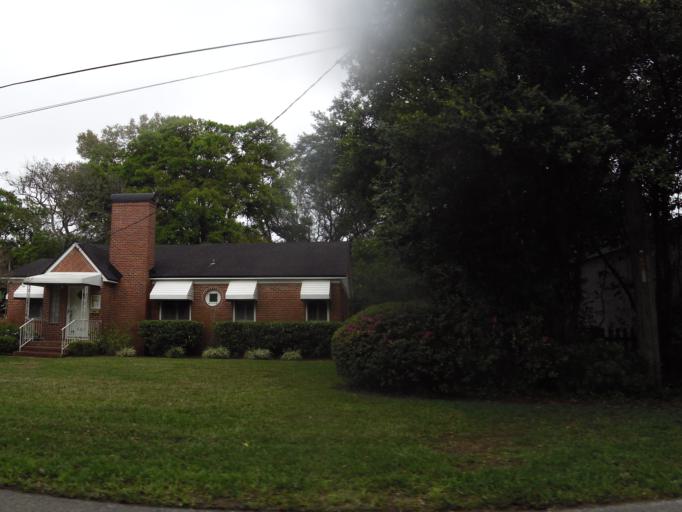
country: US
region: Florida
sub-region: Duval County
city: Jacksonville
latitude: 30.2778
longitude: -81.6519
